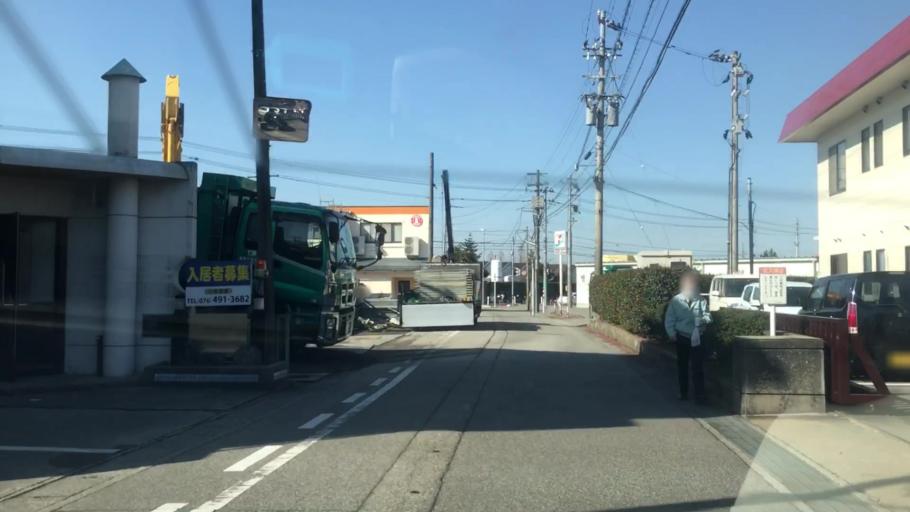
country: JP
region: Toyama
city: Toyama-shi
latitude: 36.6811
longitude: 137.2374
